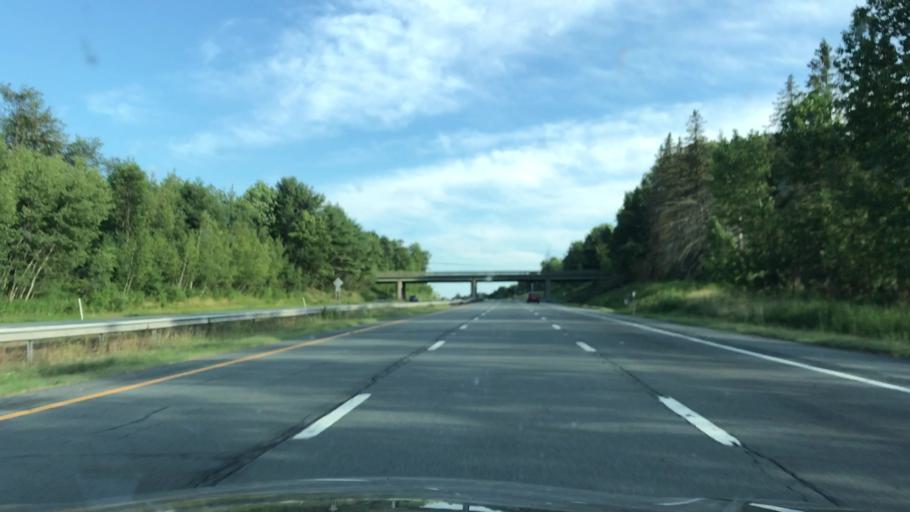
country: US
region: New York
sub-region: Sullivan County
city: Monticello
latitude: 41.6979
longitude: -74.7343
